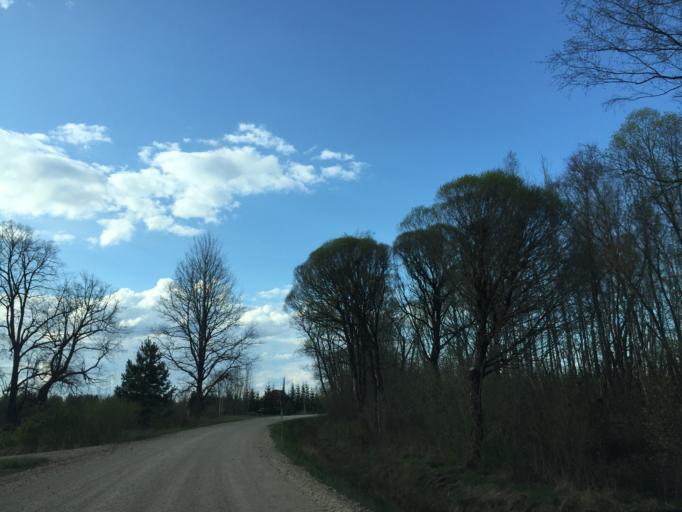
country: LV
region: Beverina
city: Murmuiza
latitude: 57.3768
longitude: 25.4871
